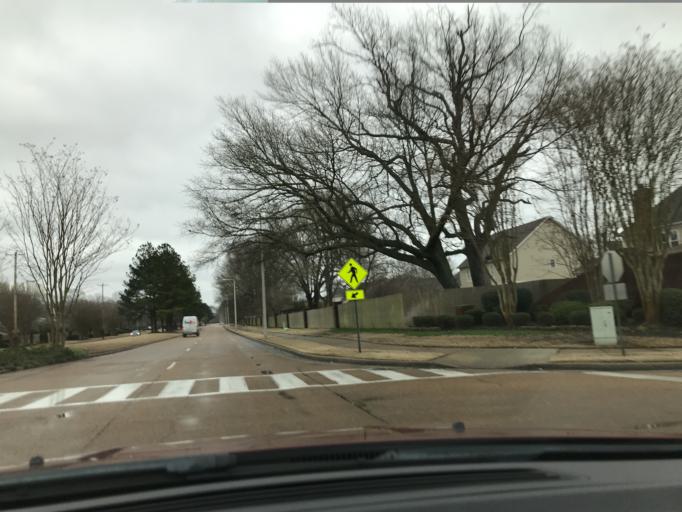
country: US
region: Tennessee
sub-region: Shelby County
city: Collierville
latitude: 35.0853
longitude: -89.6925
